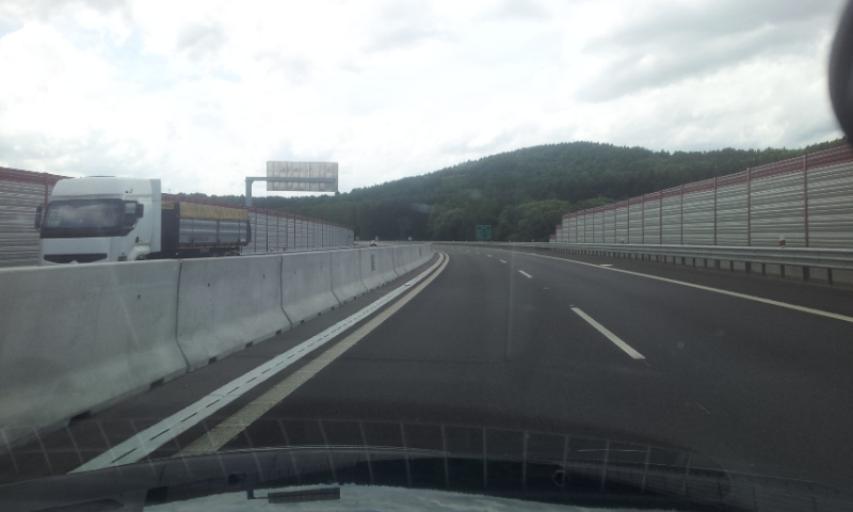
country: SK
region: Banskobystricky
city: Detva
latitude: 48.5374
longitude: 19.4453
